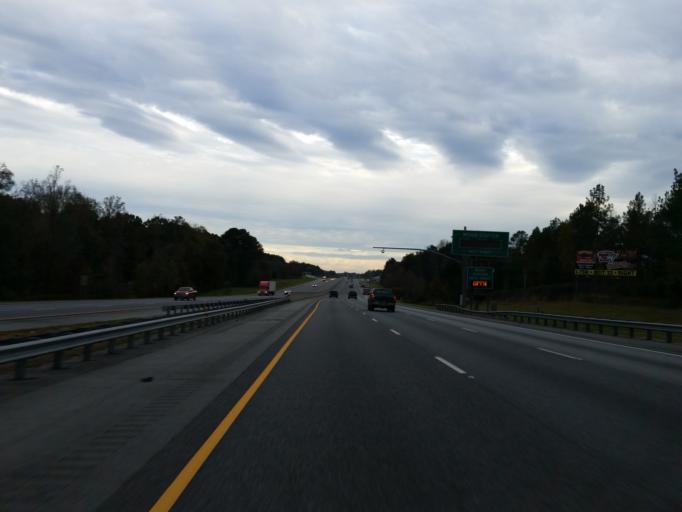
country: US
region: Georgia
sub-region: Lowndes County
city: Hahira
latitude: 30.9276
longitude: -83.3683
